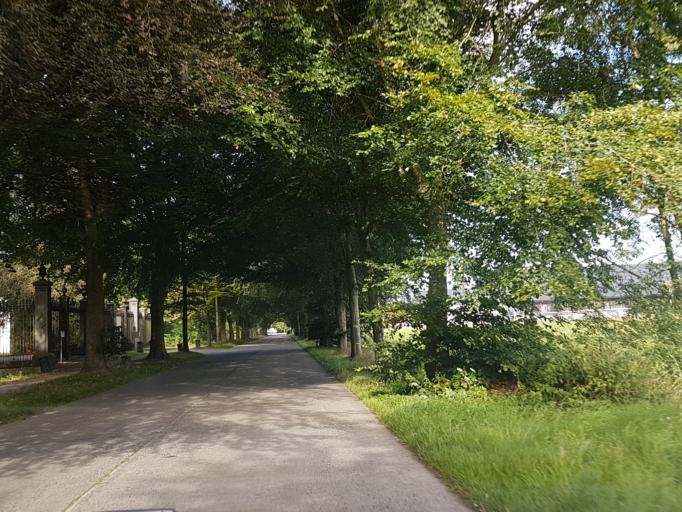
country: BE
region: Flanders
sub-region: Provincie Oost-Vlaanderen
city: Aalter
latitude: 51.0871
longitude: 3.4953
